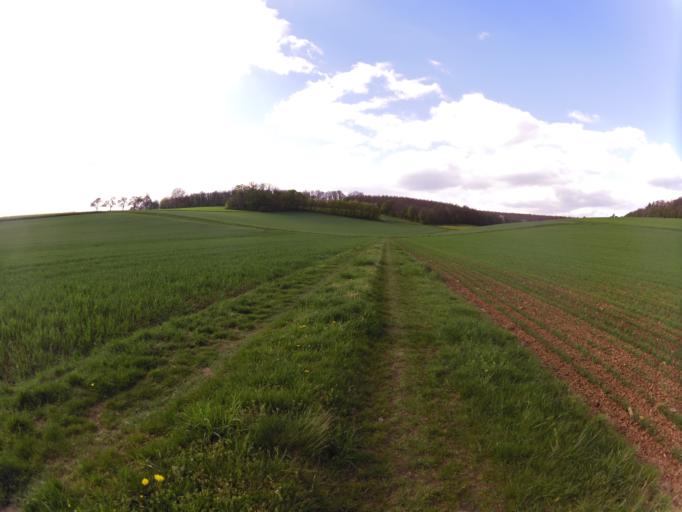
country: DE
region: Bavaria
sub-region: Regierungsbezirk Unterfranken
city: Waldbrunn
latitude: 49.7834
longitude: 9.7806
